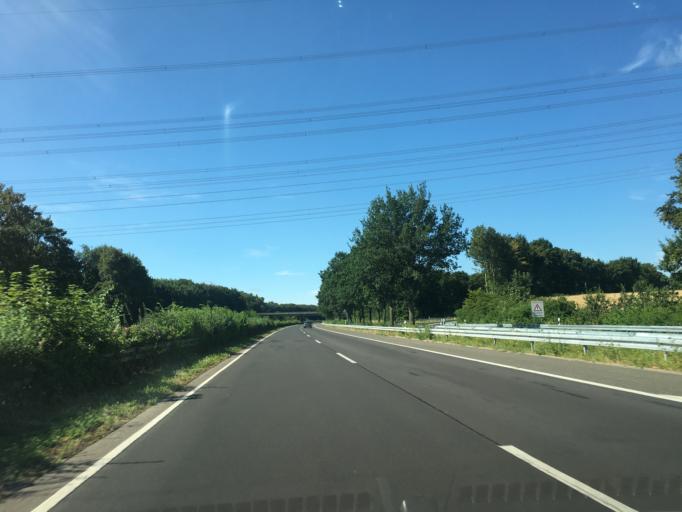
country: DE
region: North Rhine-Westphalia
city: Julich
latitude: 50.9167
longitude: 6.3273
